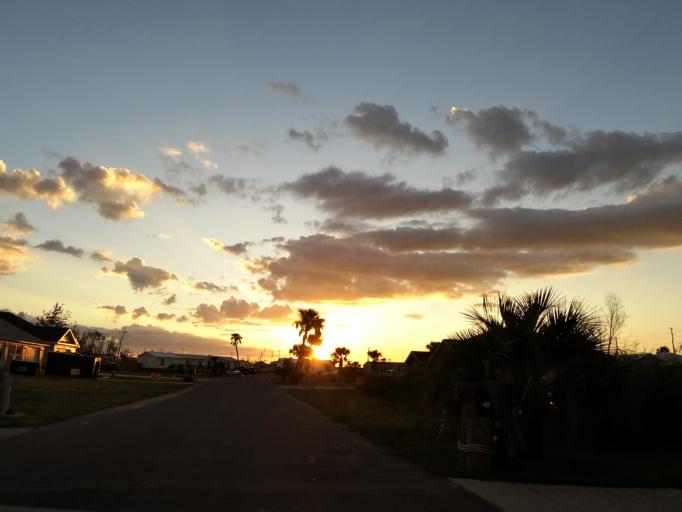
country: US
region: Florida
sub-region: Bay County
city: Mexico Beach
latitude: 29.9398
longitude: -85.3900
